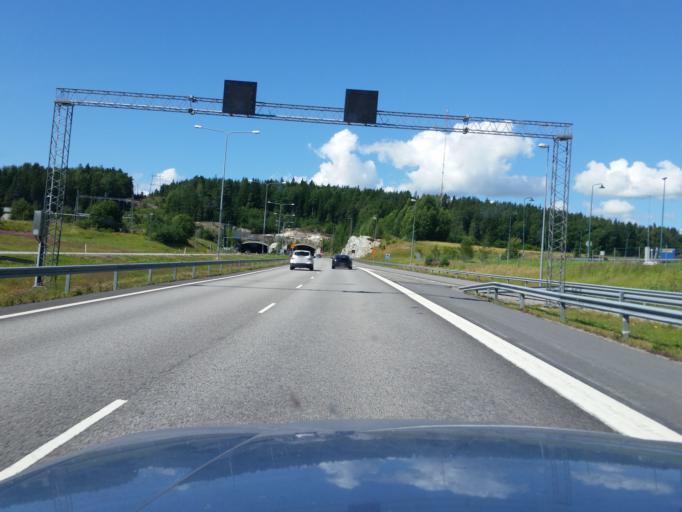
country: FI
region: Varsinais-Suomi
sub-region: Salo
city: Salo
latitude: 60.4179
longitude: 23.1641
